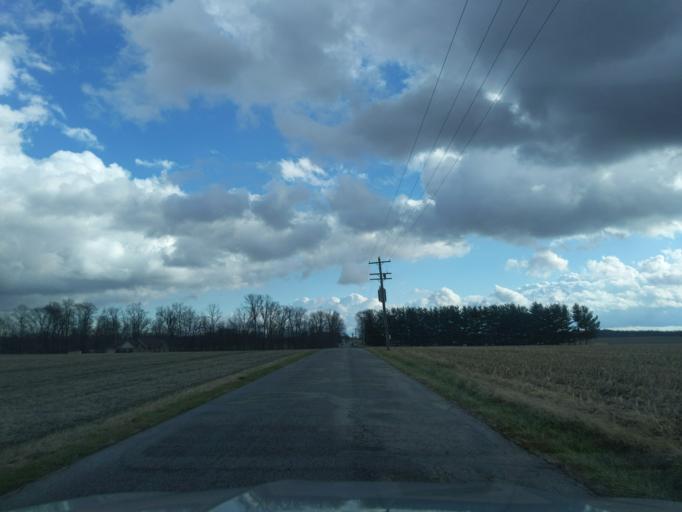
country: US
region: Indiana
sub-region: Decatur County
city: Saint Paul
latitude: 39.4093
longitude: -85.5522
